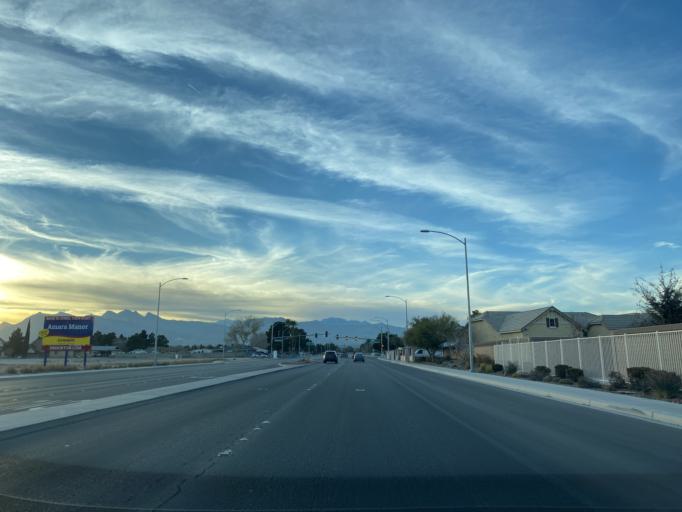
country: US
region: Nevada
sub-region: Clark County
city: Las Vegas
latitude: 36.2619
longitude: -115.2321
